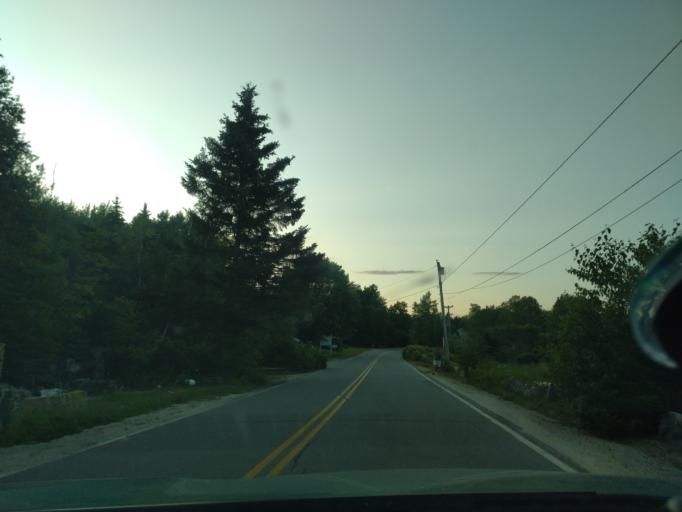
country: US
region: Maine
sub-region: Hancock County
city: Gouldsboro
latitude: 44.3653
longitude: -68.0386
